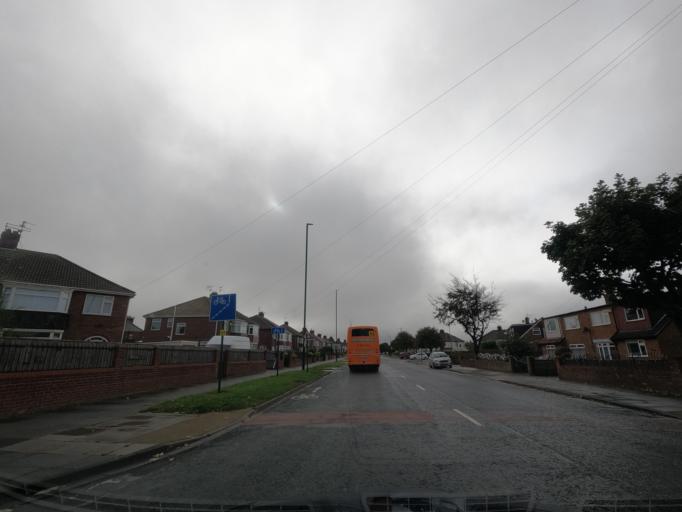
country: GB
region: England
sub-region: Redcar and Cleveland
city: Redcar
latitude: 54.6112
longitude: -1.0840
